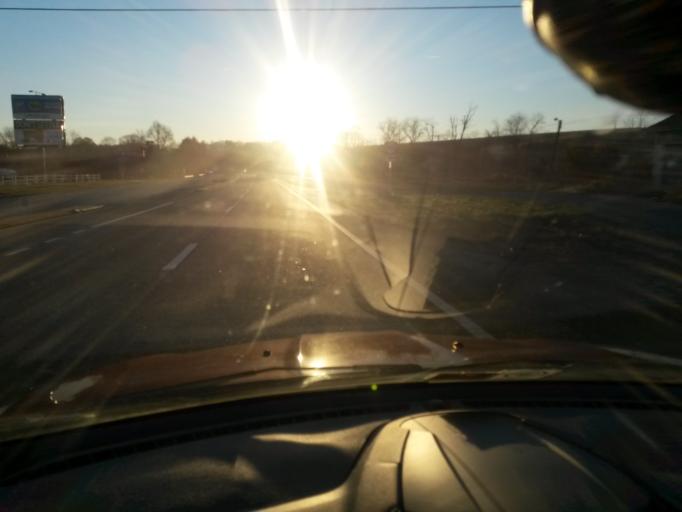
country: US
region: Virginia
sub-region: Franklin County
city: Rocky Mount
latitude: 37.0756
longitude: -79.9126
